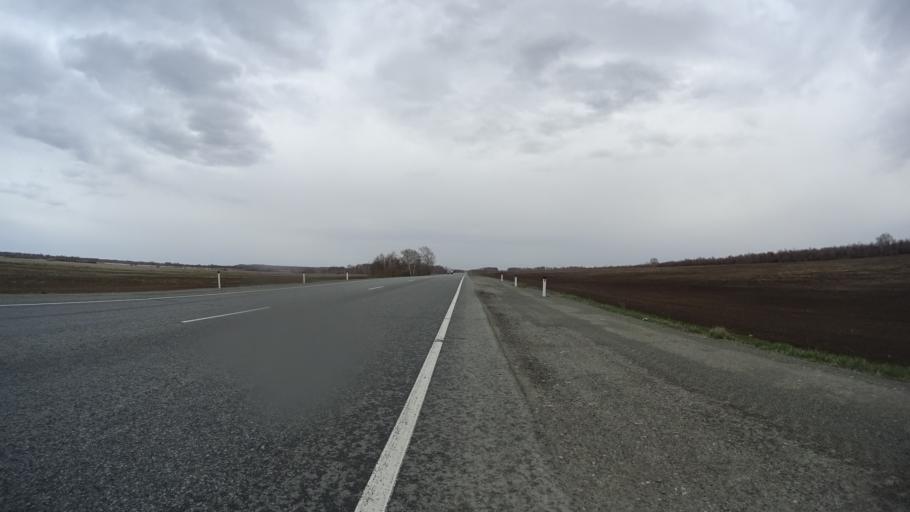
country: RU
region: Chelyabinsk
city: Krasnogorskiy
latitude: 54.6666
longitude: 61.2523
